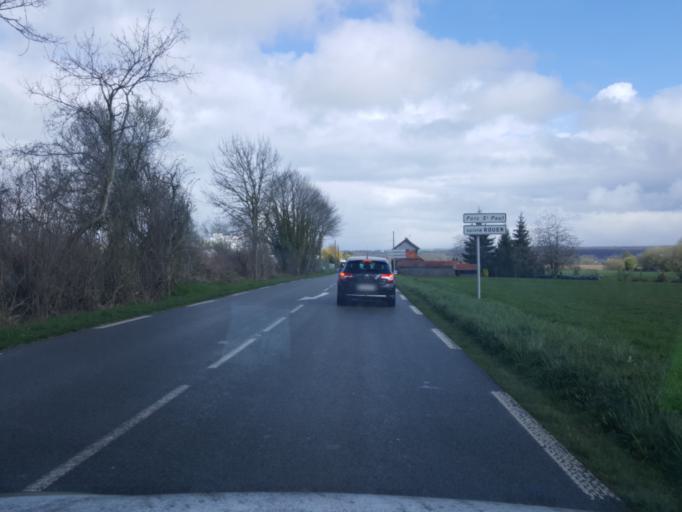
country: FR
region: Picardie
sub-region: Departement de l'Oise
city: Auneuil
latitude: 49.3800
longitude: 1.9956
